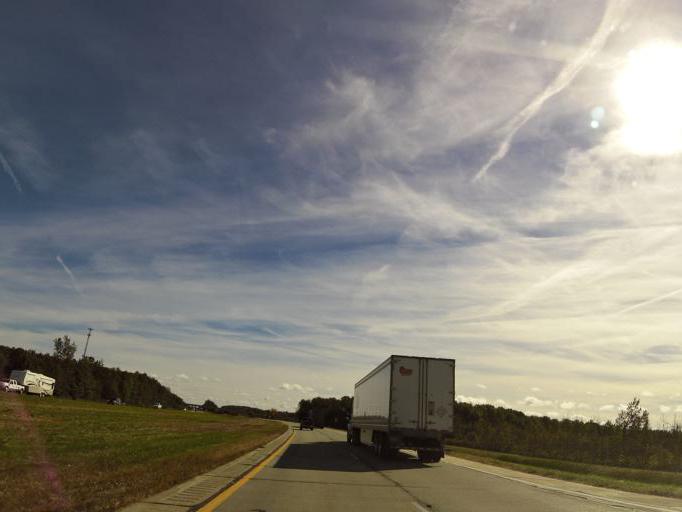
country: US
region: Michigan
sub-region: Saint Clair County
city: Capac
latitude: 42.9766
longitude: -82.8331
